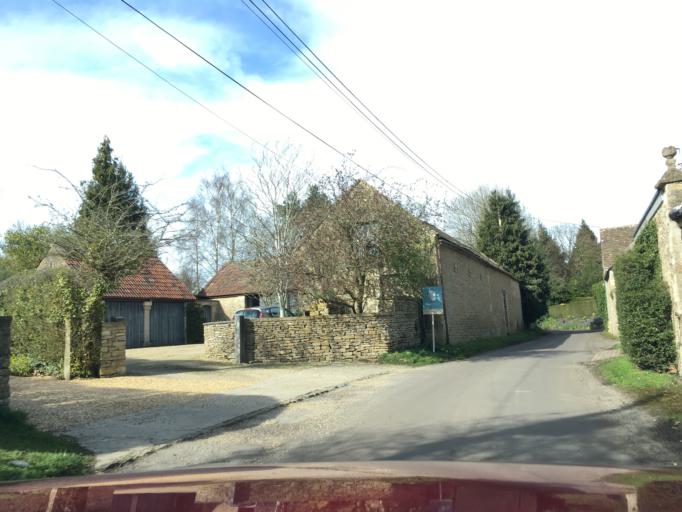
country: GB
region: England
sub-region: Wiltshire
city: Chippenham
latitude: 51.4919
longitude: -2.1138
